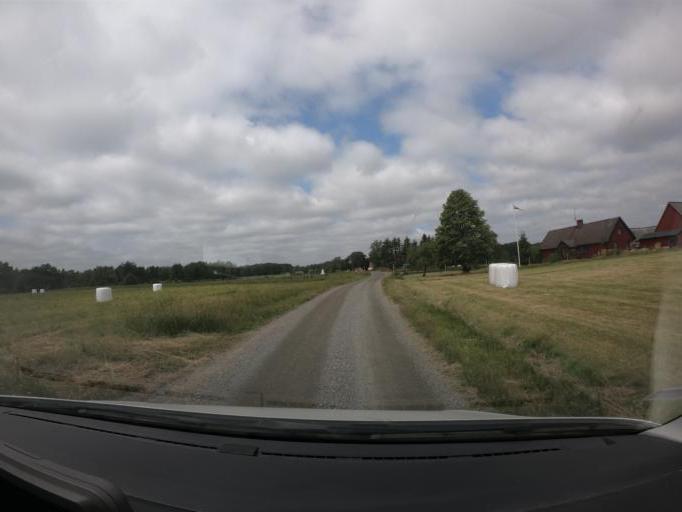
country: SE
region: Skane
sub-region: Hassleholms Kommun
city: Sosdala
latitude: 56.1042
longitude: 13.6600
